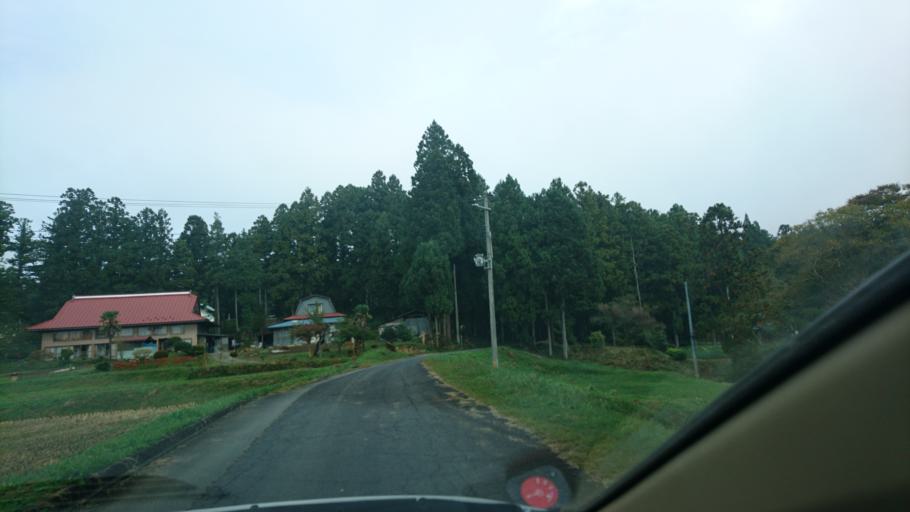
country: JP
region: Iwate
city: Ichinoseki
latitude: 38.9599
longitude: 141.1808
